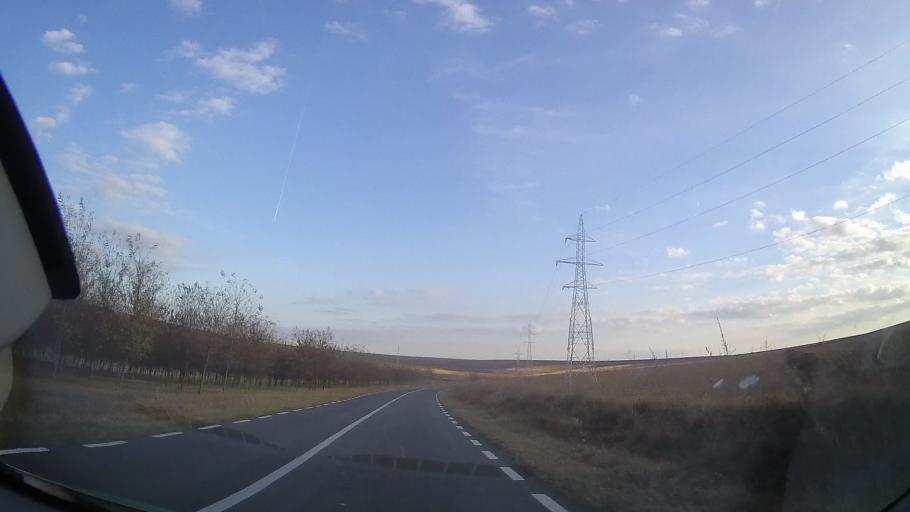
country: RO
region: Constanta
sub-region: Comuna Chirnogeni
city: Plopeni
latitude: 43.9570
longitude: 28.1482
